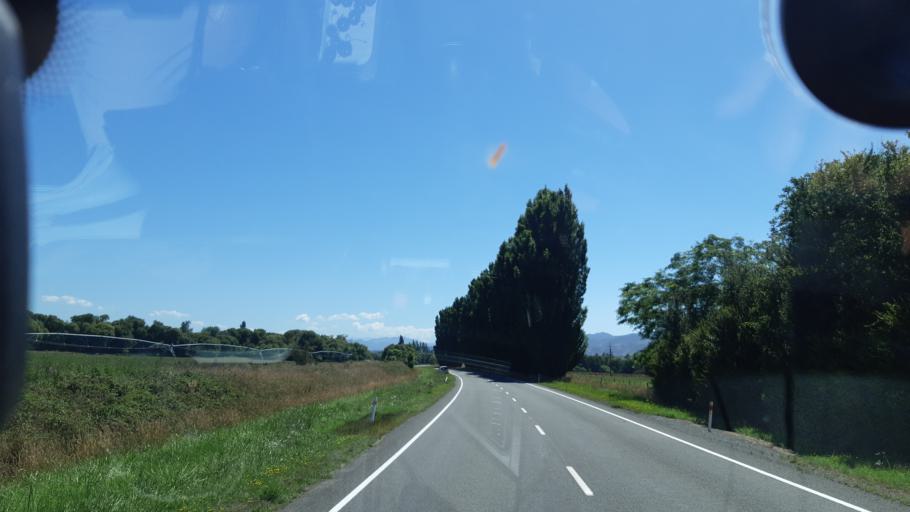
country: NZ
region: Canterbury
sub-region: Kaikoura District
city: Kaikoura
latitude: -42.7342
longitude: 173.2729
